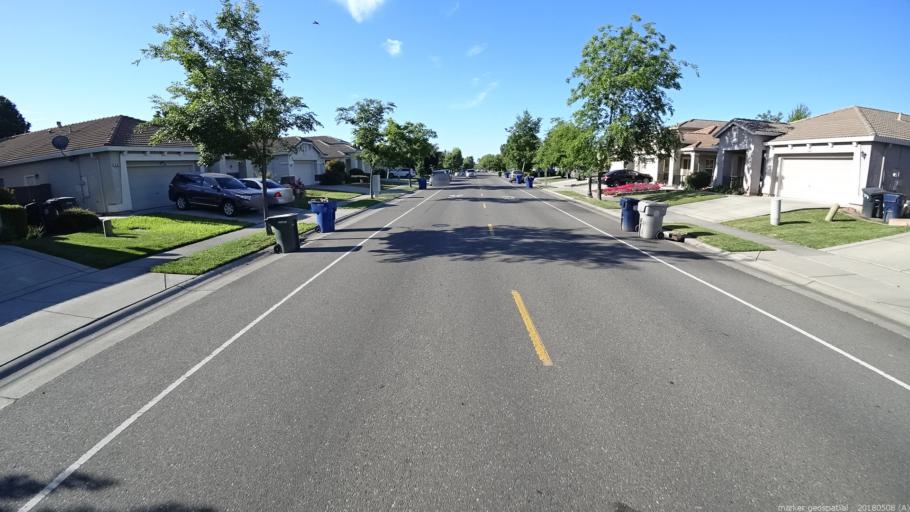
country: US
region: California
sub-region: Sacramento County
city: Elverta
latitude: 38.6797
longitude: -121.5044
